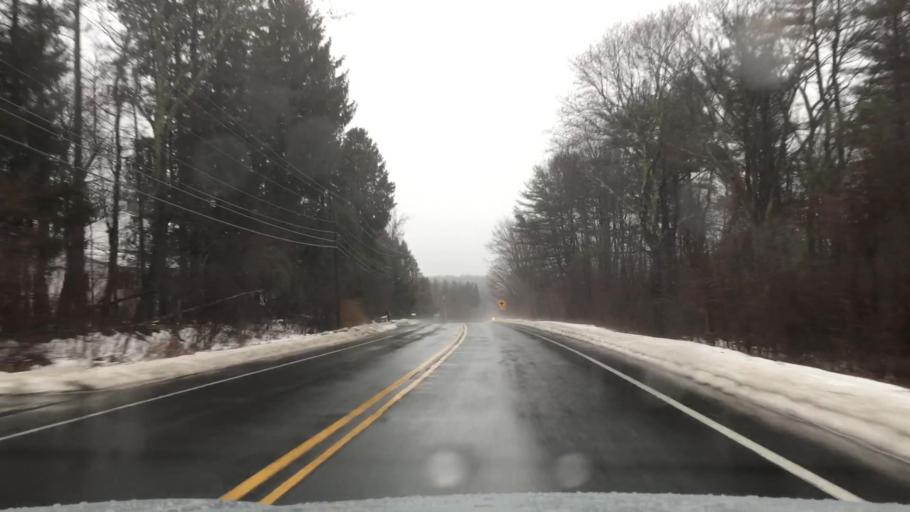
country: US
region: Massachusetts
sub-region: Hampshire County
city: Pelham
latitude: 42.3902
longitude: -72.4029
